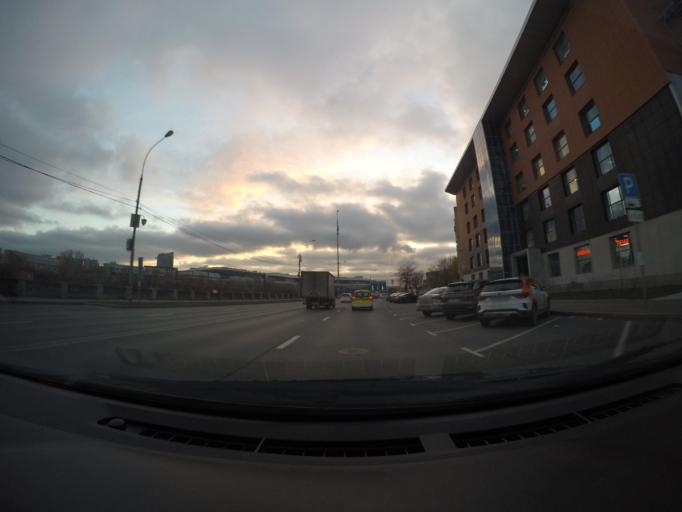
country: RU
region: Moskovskaya
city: Kozhukhovo
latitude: 55.7087
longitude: 37.6464
